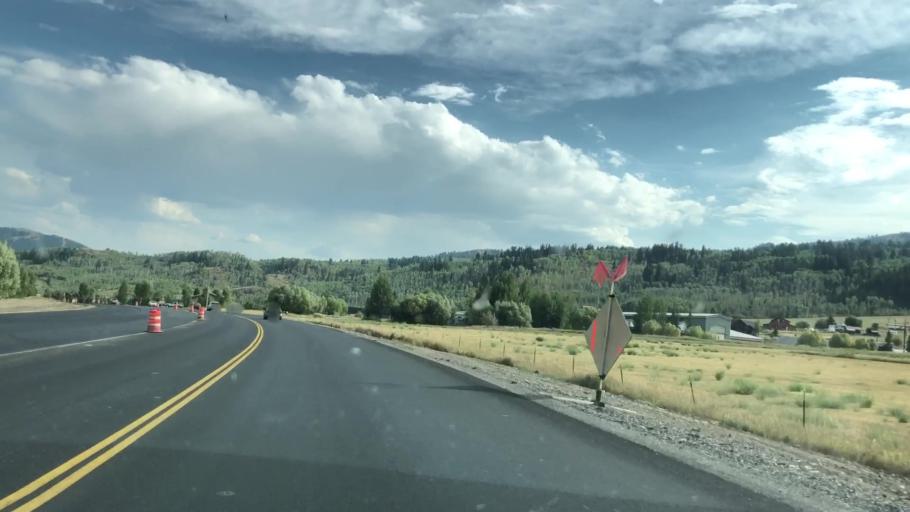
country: US
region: Wyoming
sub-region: Teton County
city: South Park
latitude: 43.3750
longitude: -110.7447
